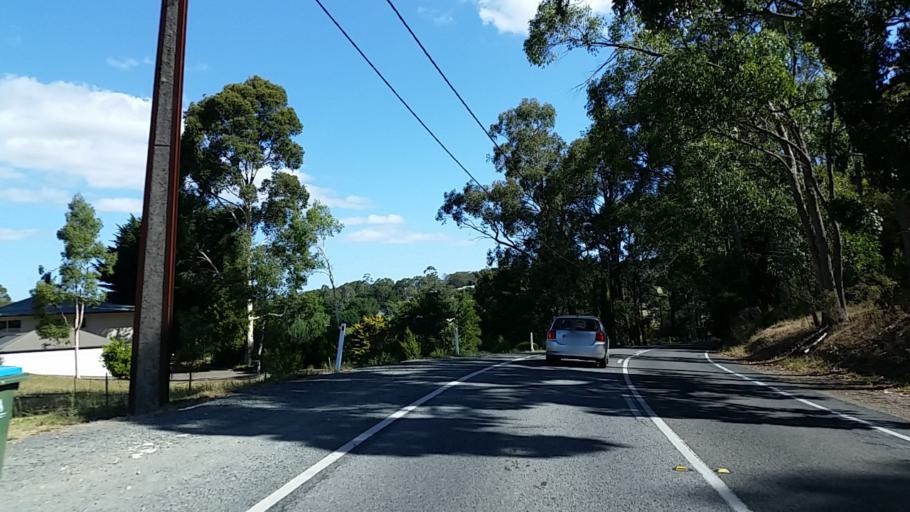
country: AU
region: South Australia
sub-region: Adelaide Hills
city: Bridgewater
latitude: -34.9741
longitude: 138.7306
